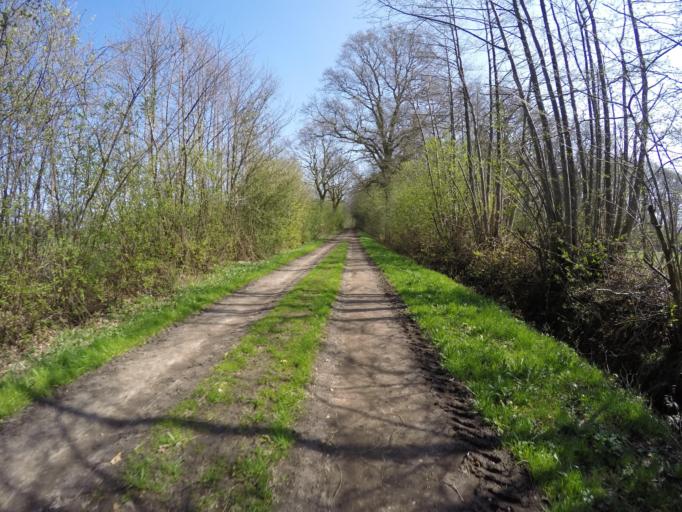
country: DE
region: Schleswig-Holstein
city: Hemdingen
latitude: 53.7459
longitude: 9.8181
